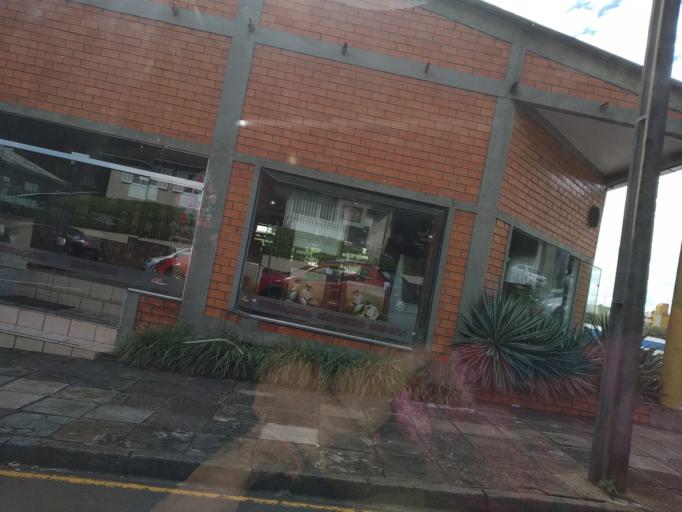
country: BR
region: Parana
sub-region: Pato Branco
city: Pato Branco
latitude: -26.2303
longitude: -52.6698
